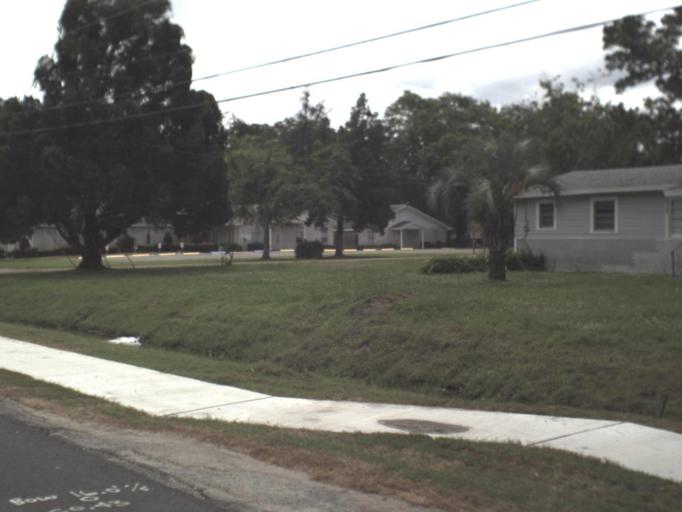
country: US
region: Florida
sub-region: Nassau County
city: Nassau Village-Ratliff
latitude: 30.4381
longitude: -81.7340
